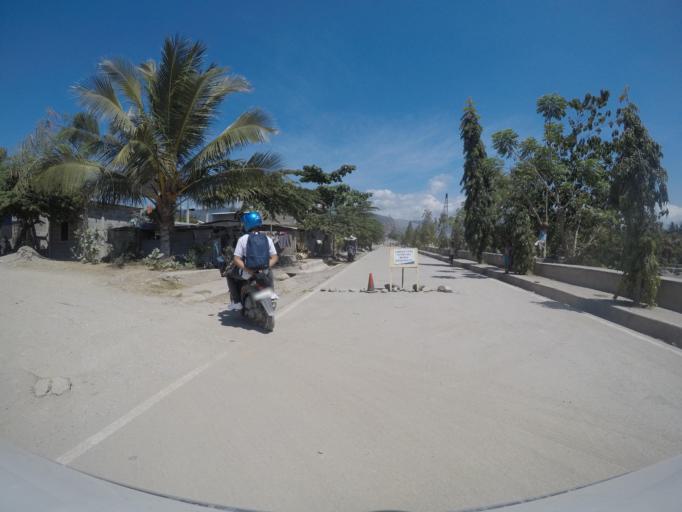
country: TL
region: Dili
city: Dili
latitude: -8.5504
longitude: 125.5369
